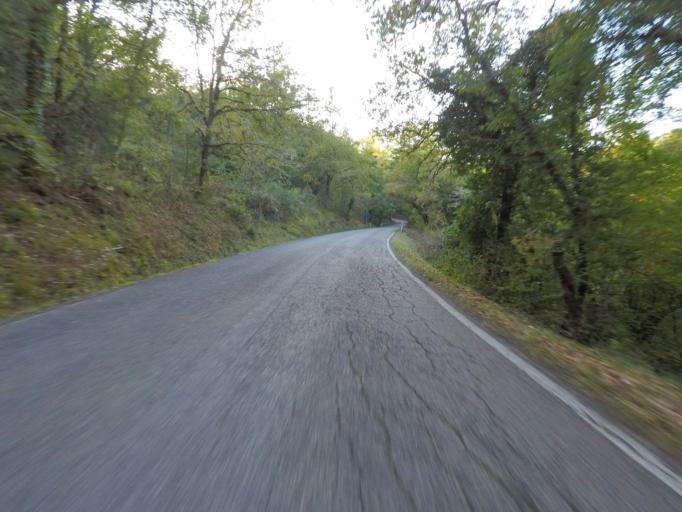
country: IT
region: Tuscany
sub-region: Provincia di Siena
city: Radda in Chianti
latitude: 43.4666
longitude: 11.3762
